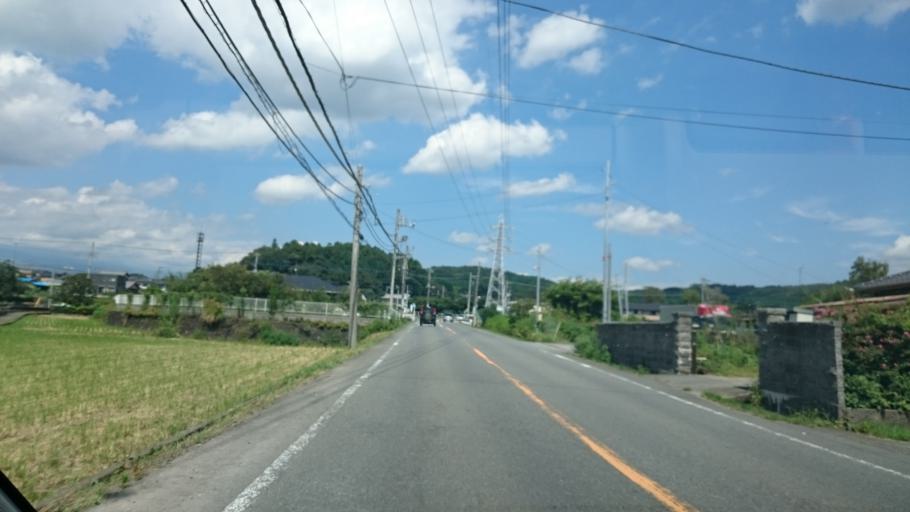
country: JP
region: Shizuoka
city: Mishima
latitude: 35.1917
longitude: 138.9222
